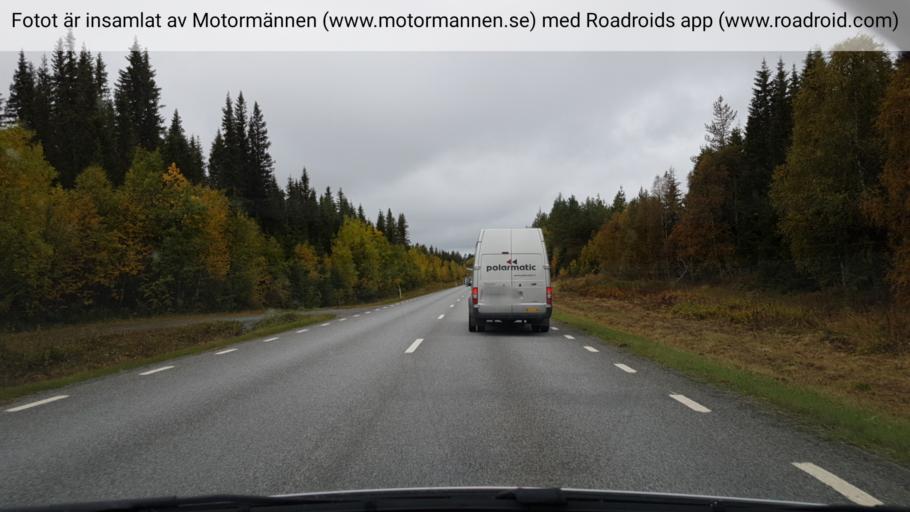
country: SE
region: Jaemtland
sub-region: OEstersunds Kommun
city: Lit
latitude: 63.4523
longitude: 15.1628
